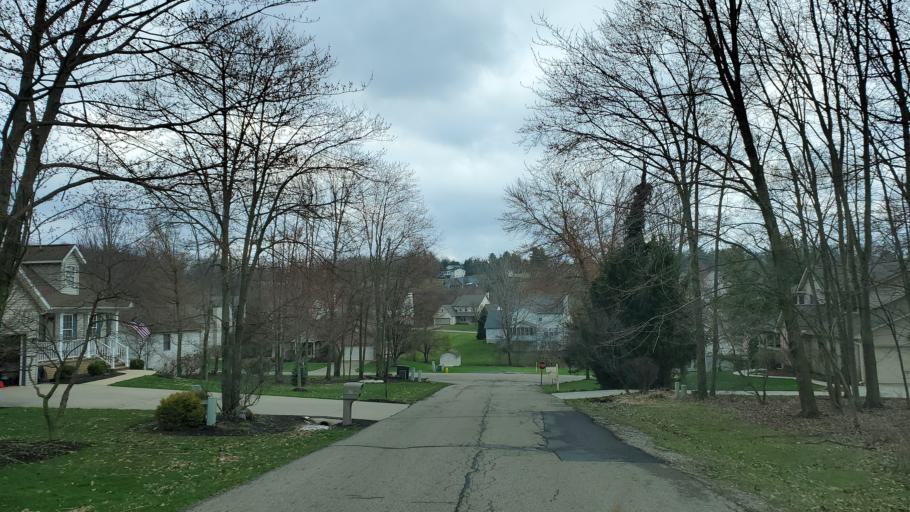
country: US
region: Ohio
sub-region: Licking County
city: Newark
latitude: 40.0339
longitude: -82.3802
